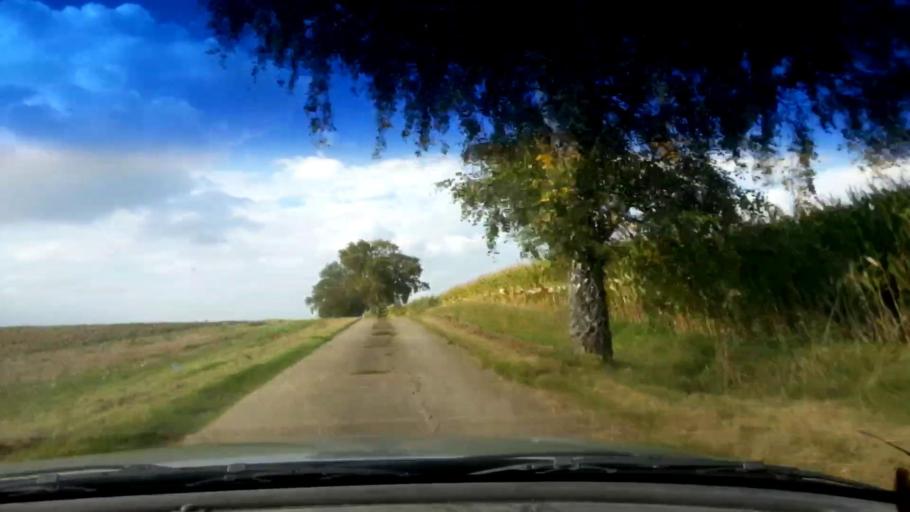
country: DE
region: Bavaria
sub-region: Upper Franconia
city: Zapfendorf
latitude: 49.9761
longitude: 10.9378
